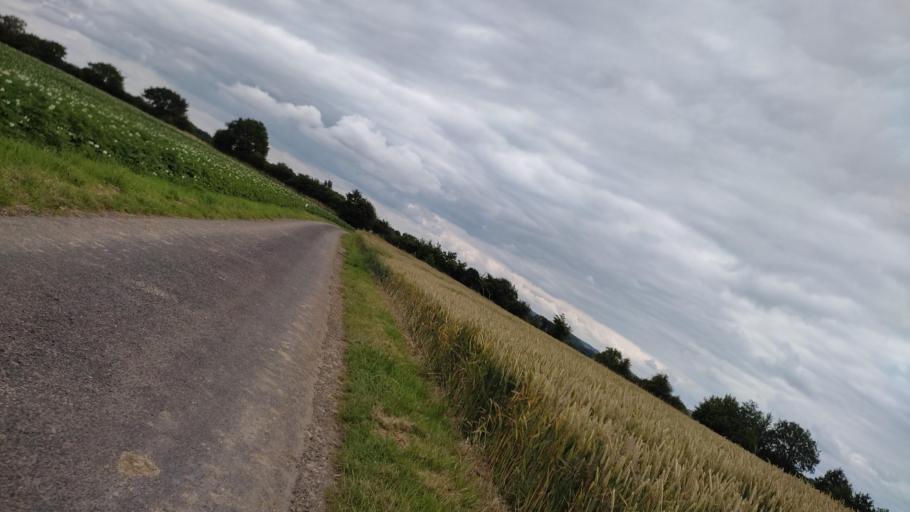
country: FR
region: Nord-Pas-de-Calais
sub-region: Departement du Pas-de-Calais
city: Beaumetz-les-Loges
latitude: 50.2321
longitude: 2.6347
